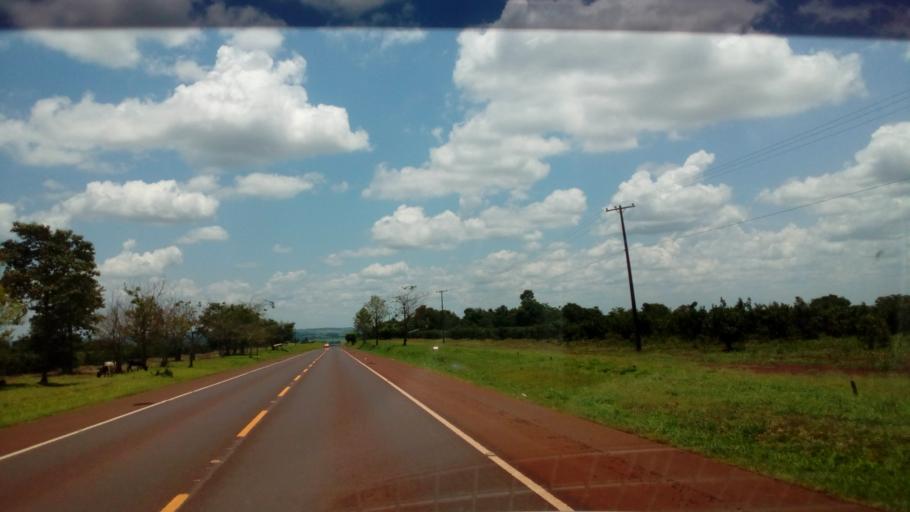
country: PY
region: Itapua
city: Edelira
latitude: -26.6558
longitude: -55.2837
